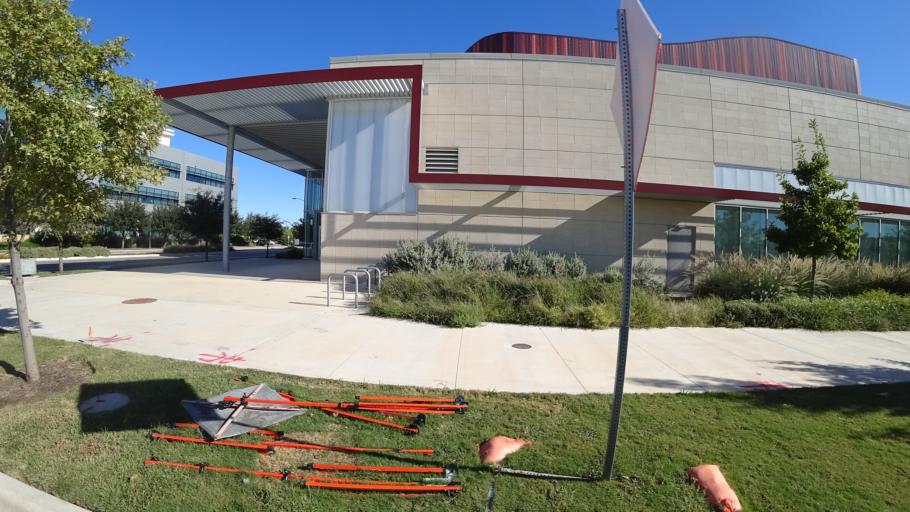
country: US
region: Texas
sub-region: Travis County
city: Austin
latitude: 30.3040
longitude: -97.7034
